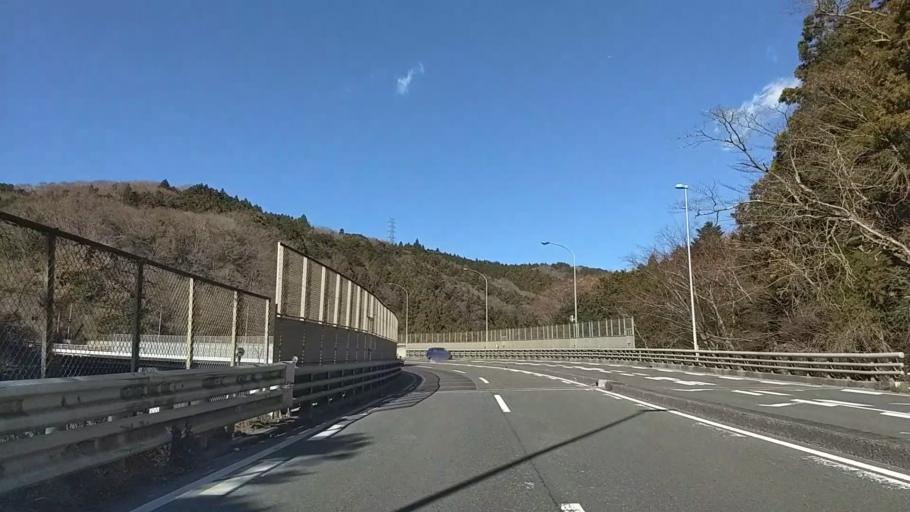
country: JP
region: Shizuoka
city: Gotemba
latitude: 35.3638
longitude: 138.9987
